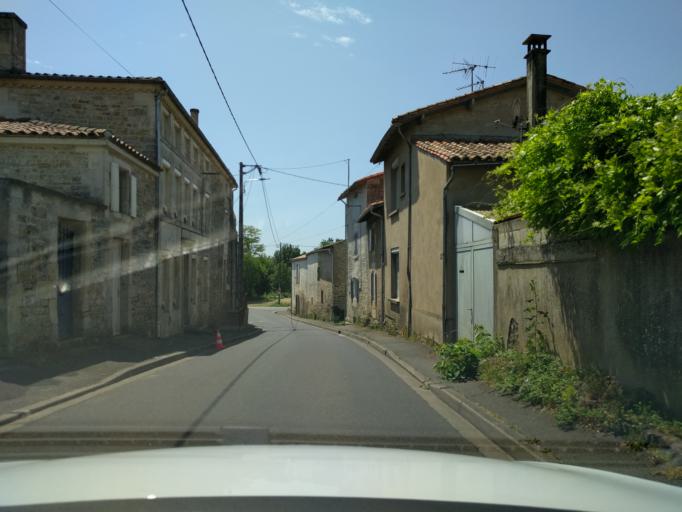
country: FR
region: Poitou-Charentes
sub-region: Departement des Deux-Sevres
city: Niort
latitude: 46.3416
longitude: -0.4643
